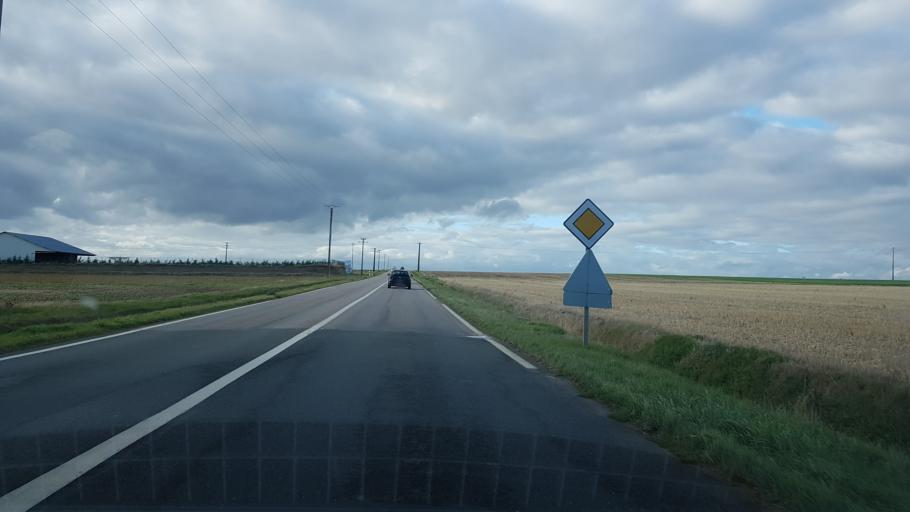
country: FR
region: Ile-de-France
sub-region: Departement de l'Essonne
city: Saclas
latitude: 48.3491
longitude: 2.1763
